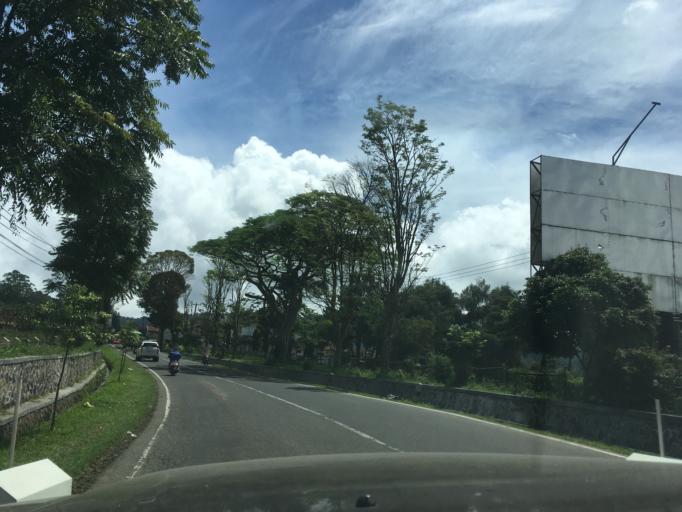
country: ID
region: West Java
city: Lembang
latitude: -6.7998
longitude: 107.6519
